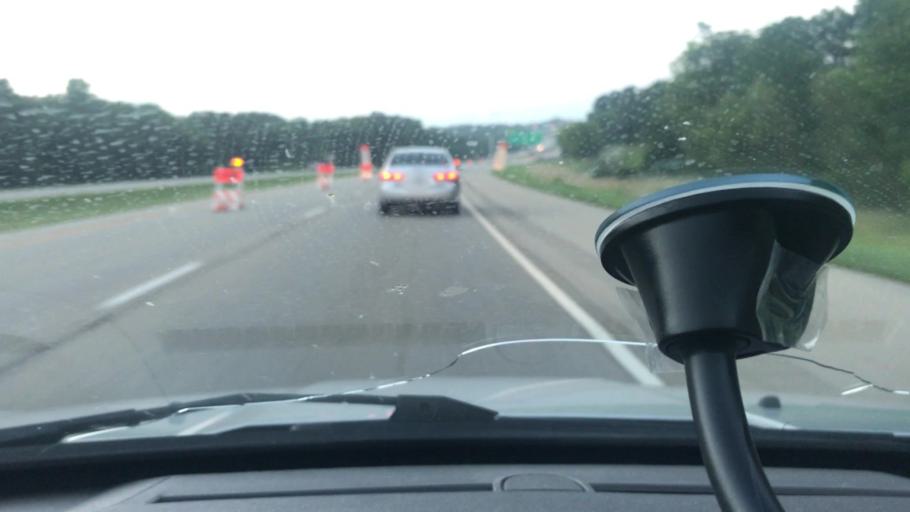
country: US
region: Illinois
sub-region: Peoria County
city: Bellevue
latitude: 40.7239
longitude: -89.6761
